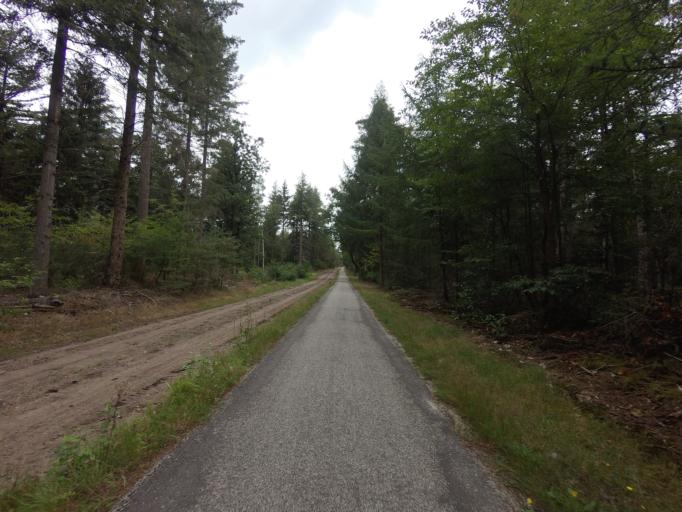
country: NL
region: Overijssel
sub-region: Gemeente Hof van Twente
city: Markelo
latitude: 52.3063
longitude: 6.4532
